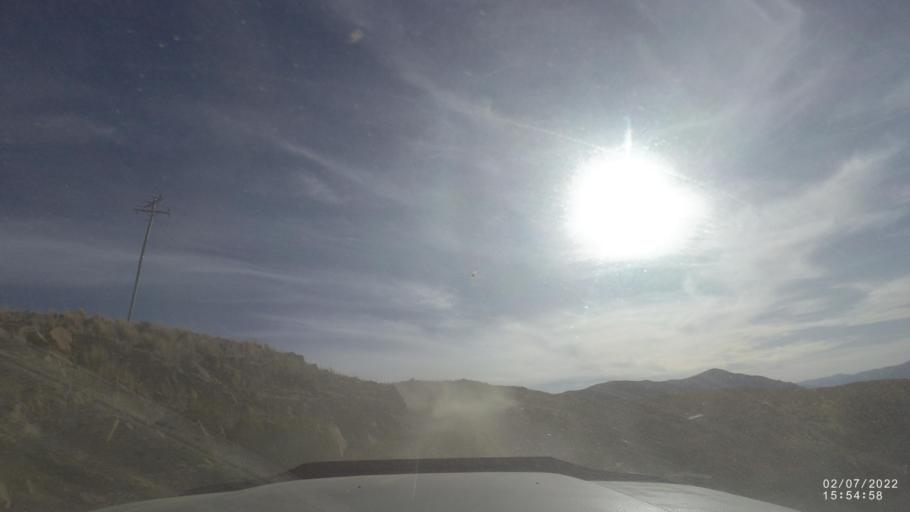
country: BO
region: Cochabamba
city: Irpa Irpa
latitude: -17.9088
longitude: -66.4196
